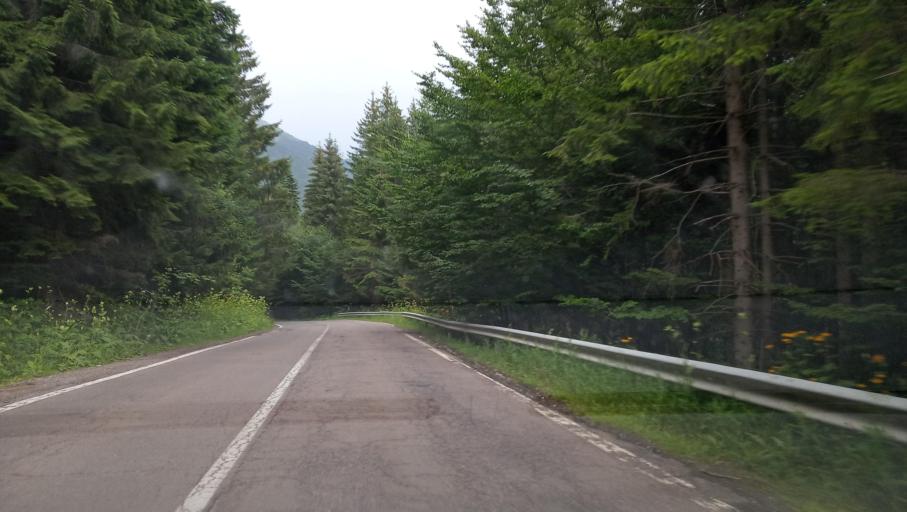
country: RO
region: Prahova
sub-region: Oras Sinaia
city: Sinaia
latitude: 45.3228
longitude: 25.5184
